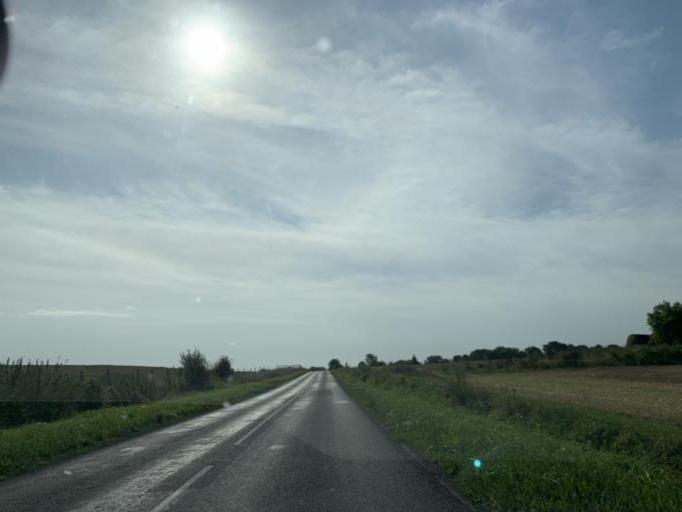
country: FR
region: Ile-de-France
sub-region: Departement de Seine-et-Marne
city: Annet-sur-Marne
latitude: 48.9339
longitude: 2.7108
